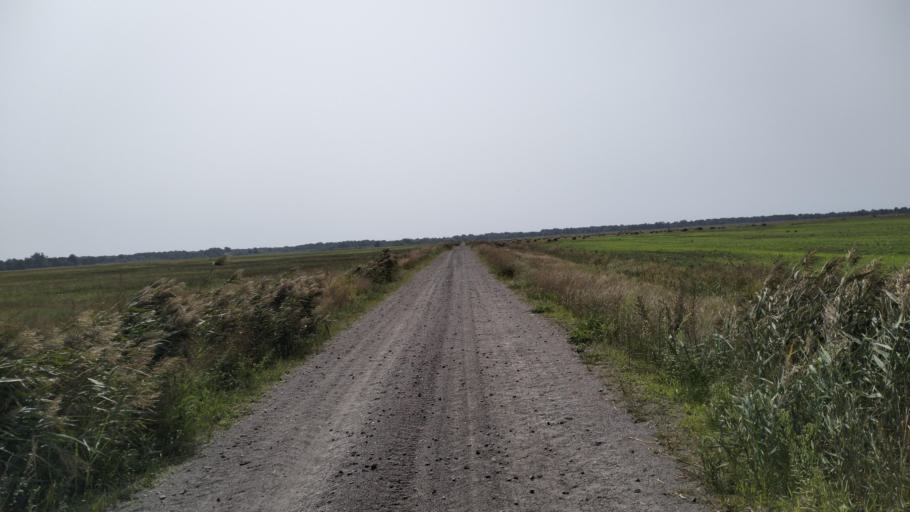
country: BY
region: Brest
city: Davyd-Haradok
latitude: 51.9841
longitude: 27.1752
